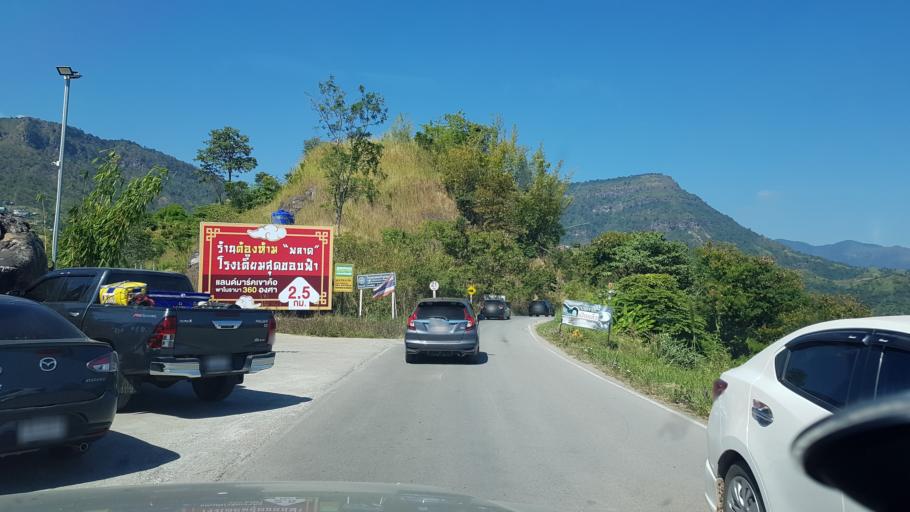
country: TH
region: Phetchabun
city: Khao Kho
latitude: 16.7842
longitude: 101.0514
